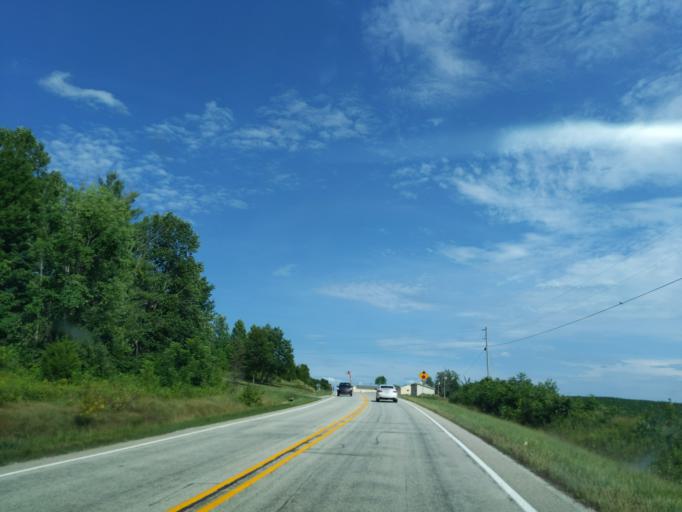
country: US
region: Indiana
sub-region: Ripley County
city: Sunman
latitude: 39.2725
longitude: -85.1031
